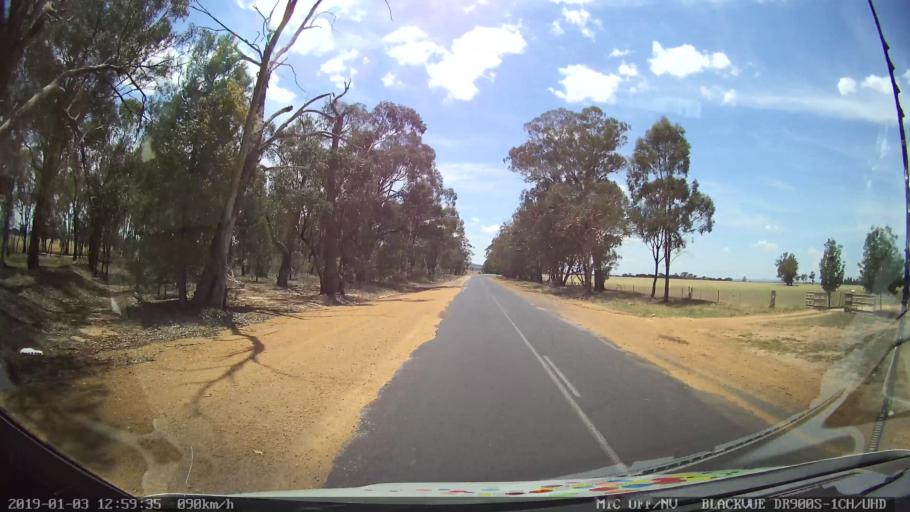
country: AU
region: New South Wales
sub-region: Cabonne
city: Canowindra
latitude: -33.6358
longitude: 148.3912
